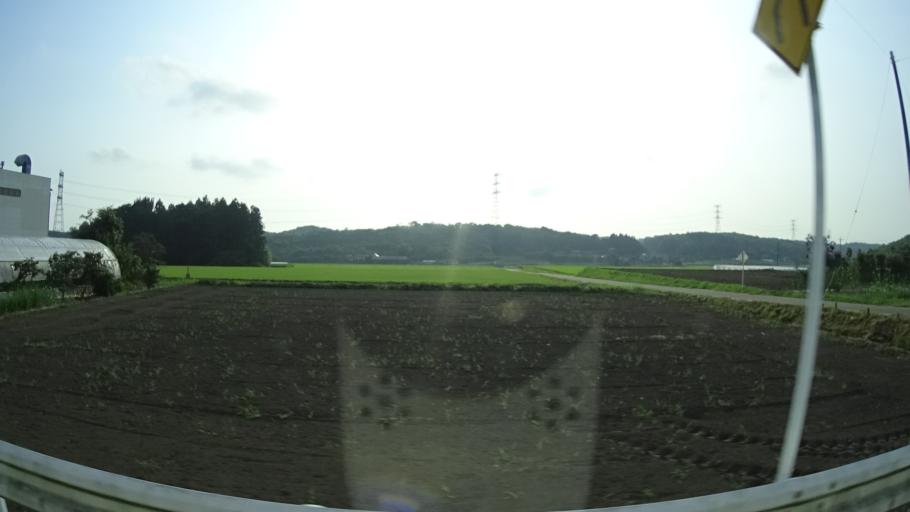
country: JP
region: Tochigi
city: Motegi
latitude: 36.5674
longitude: 140.1037
